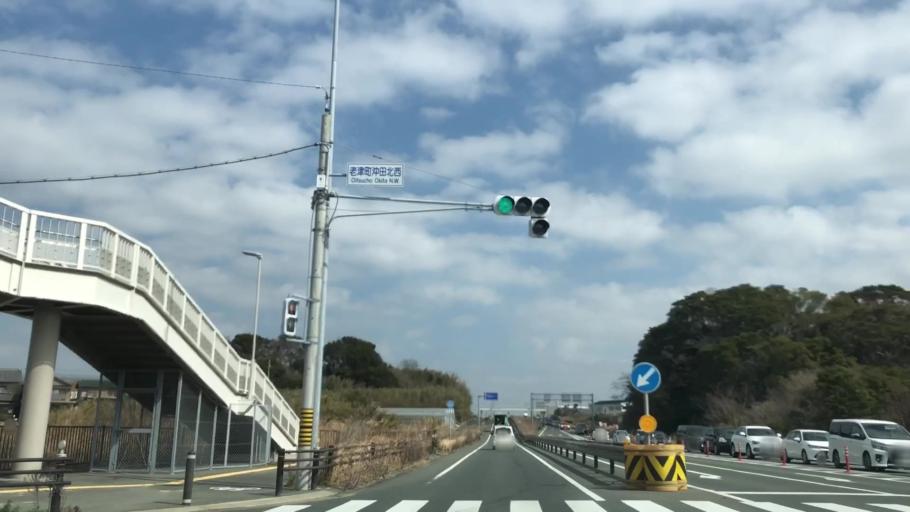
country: JP
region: Aichi
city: Tahara
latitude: 34.6935
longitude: 137.3304
